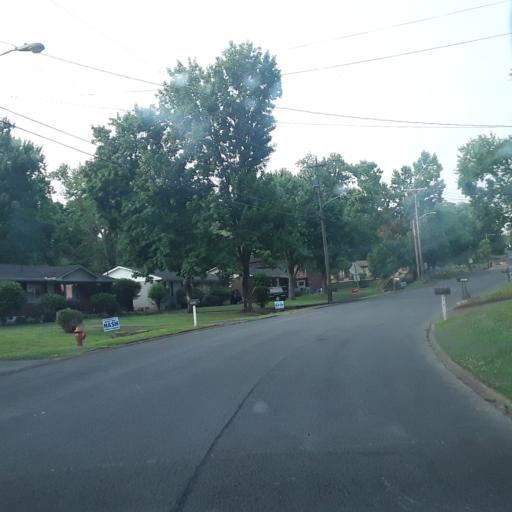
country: US
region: Tennessee
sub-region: Williamson County
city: Brentwood
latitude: 36.0564
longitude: -86.7319
